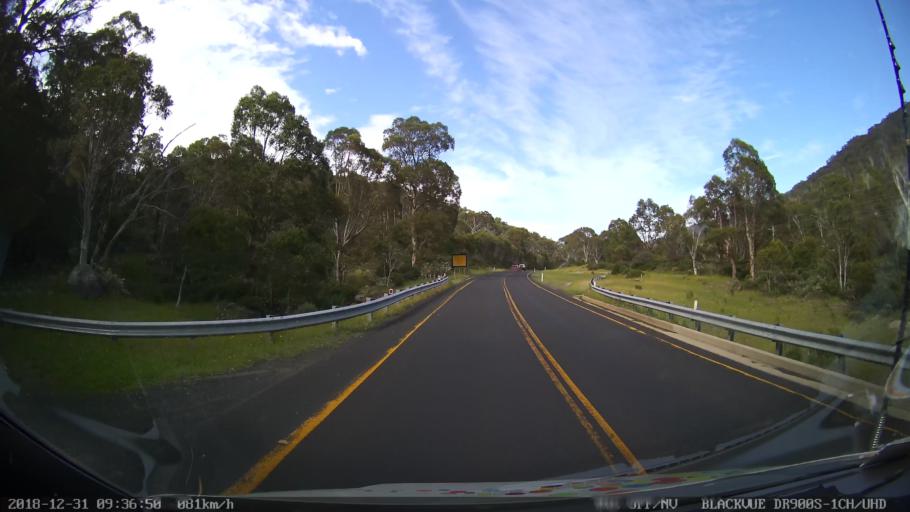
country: AU
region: New South Wales
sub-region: Snowy River
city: Jindabyne
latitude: -36.4619
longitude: 148.3824
